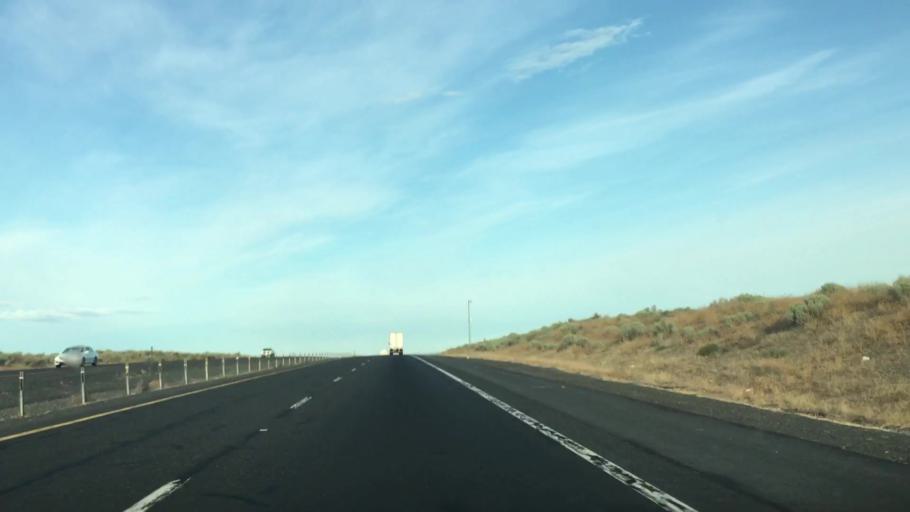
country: US
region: Washington
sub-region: Grant County
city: Cascade Valley
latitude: 47.1042
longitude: -119.4818
